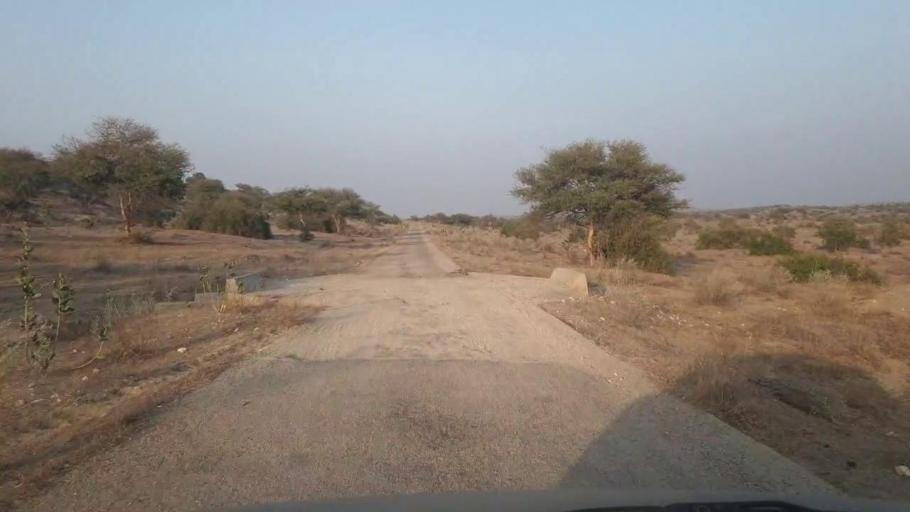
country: PK
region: Sindh
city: Umarkot
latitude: 25.2242
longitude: 69.8858
